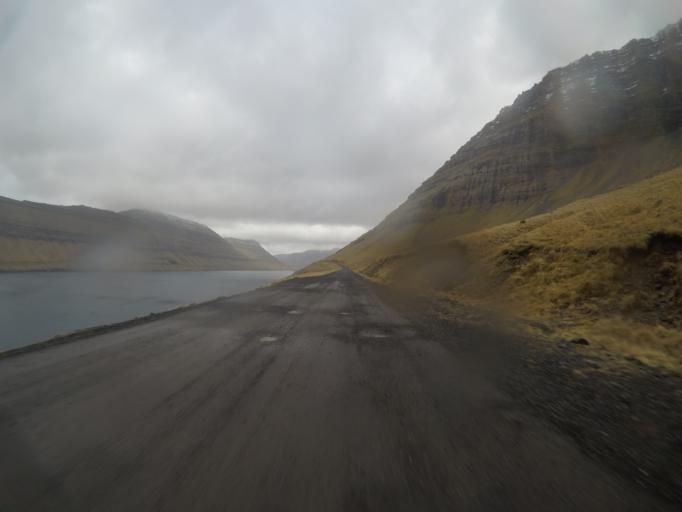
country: FO
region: Nordoyar
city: Klaksvik
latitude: 62.3351
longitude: -6.5772
